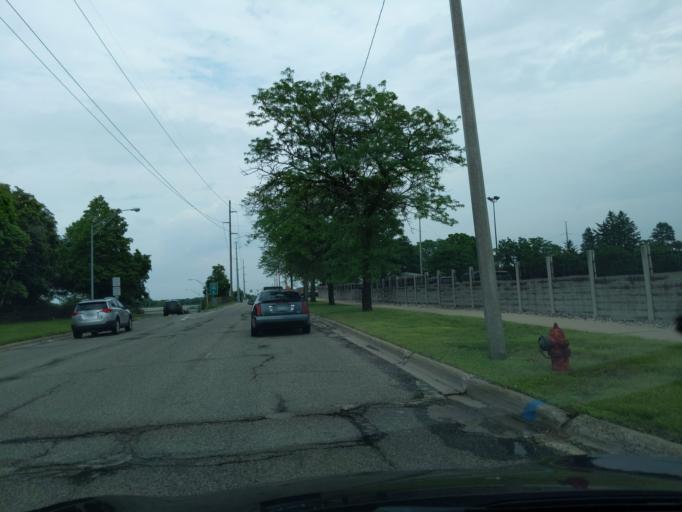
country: US
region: Michigan
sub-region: Ingham County
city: Lansing
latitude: 42.7255
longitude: -84.5570
